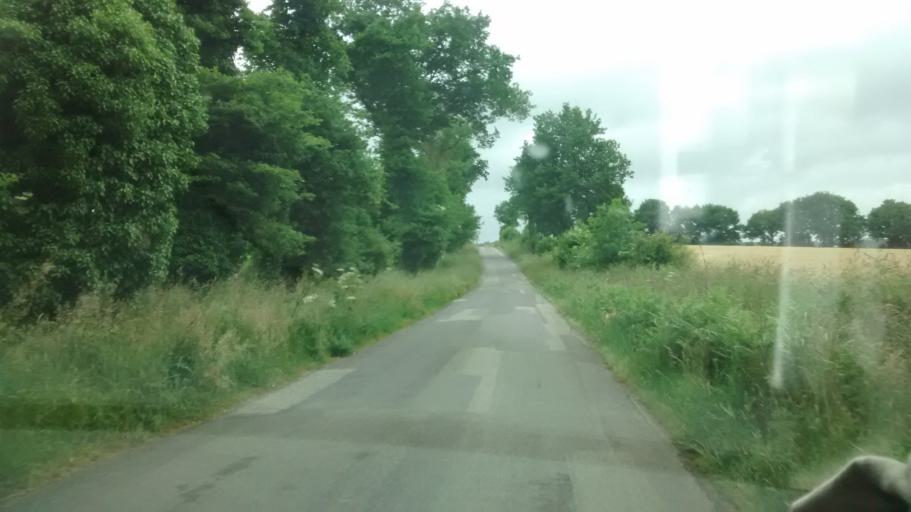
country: FR
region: Brittany
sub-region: Departement du Morbihan
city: Molac
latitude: 47.7173
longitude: -2.4597
